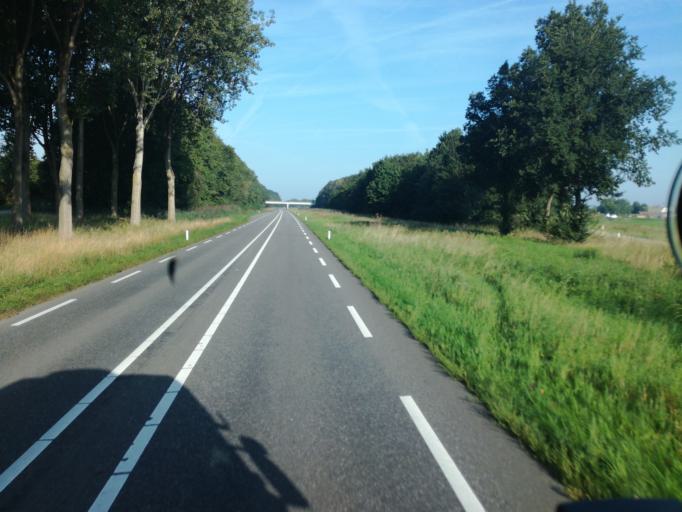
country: NL
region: North Brabant
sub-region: Gemeente Heusden
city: Heusden
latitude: 51.7208
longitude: 5.1340
